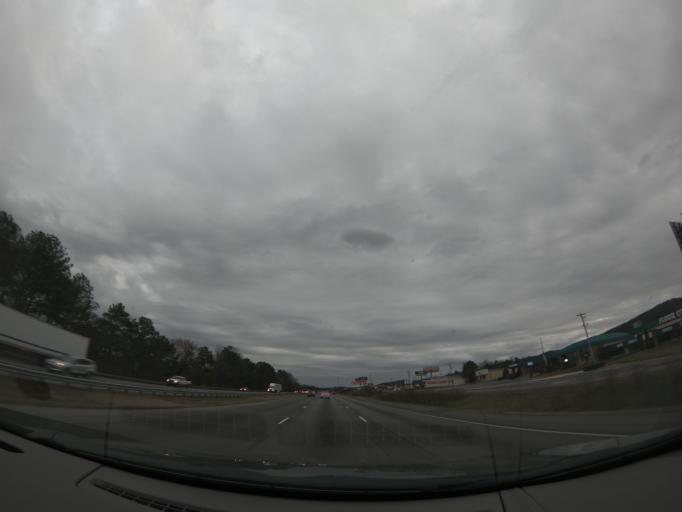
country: US
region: Georgia
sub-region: Whitfield County
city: Dalton
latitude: 34.6951
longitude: -85.0039
